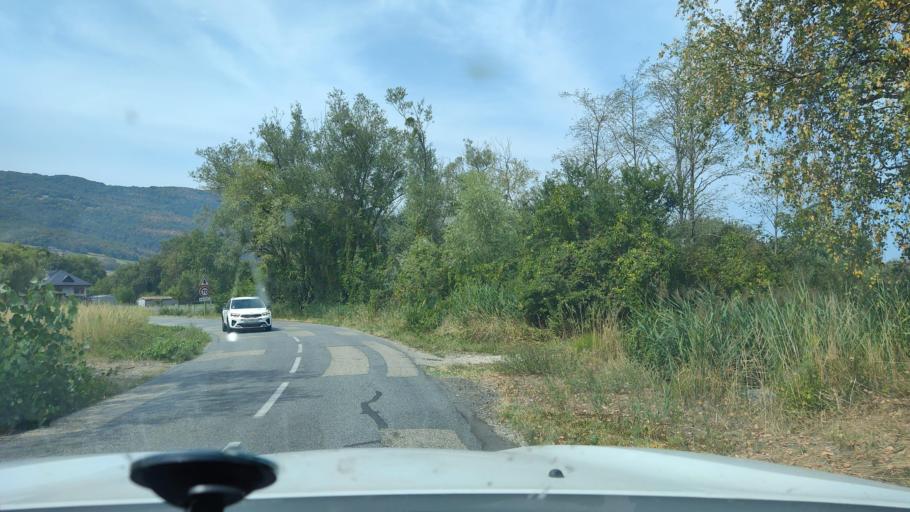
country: FR
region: Rhone-Alpes
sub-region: Departement de la Savoie
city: Saint-Baldoph
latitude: 45.5143
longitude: 5.9726
